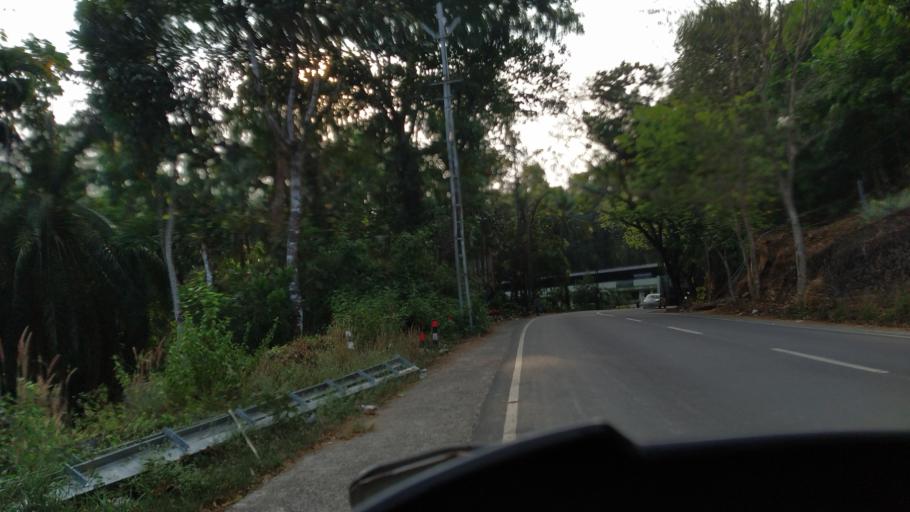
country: IN
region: Kerala
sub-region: Kottayam
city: Erattupetta
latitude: 9.5533
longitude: 76.7888
